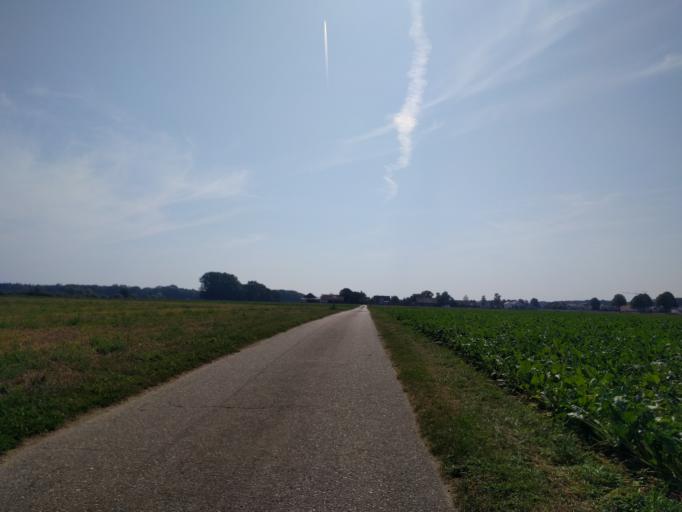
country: DE
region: Bavaria
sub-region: Upper Palatinate
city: Mintraching
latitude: 48.9897
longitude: 12.2496
